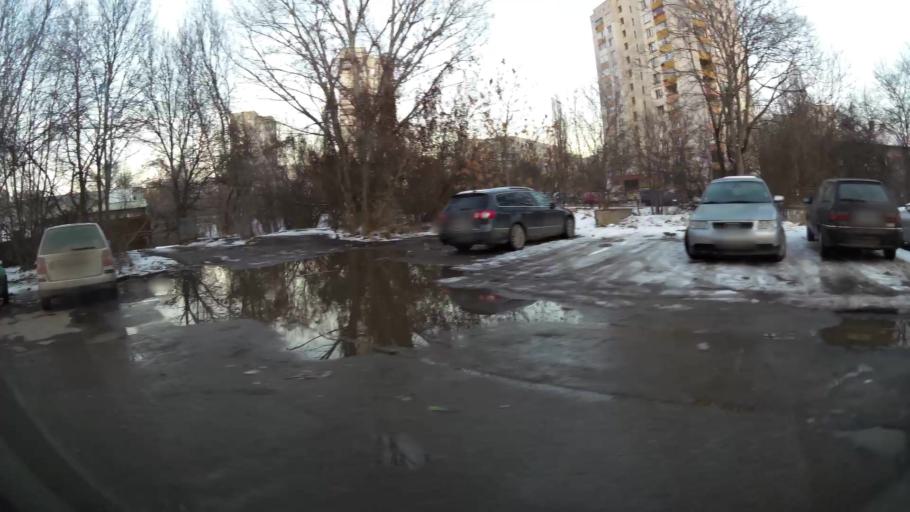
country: BG
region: Sofia-Capital
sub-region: Stolichna Obshtina
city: Sofia
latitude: 42.6809
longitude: 23.3745
